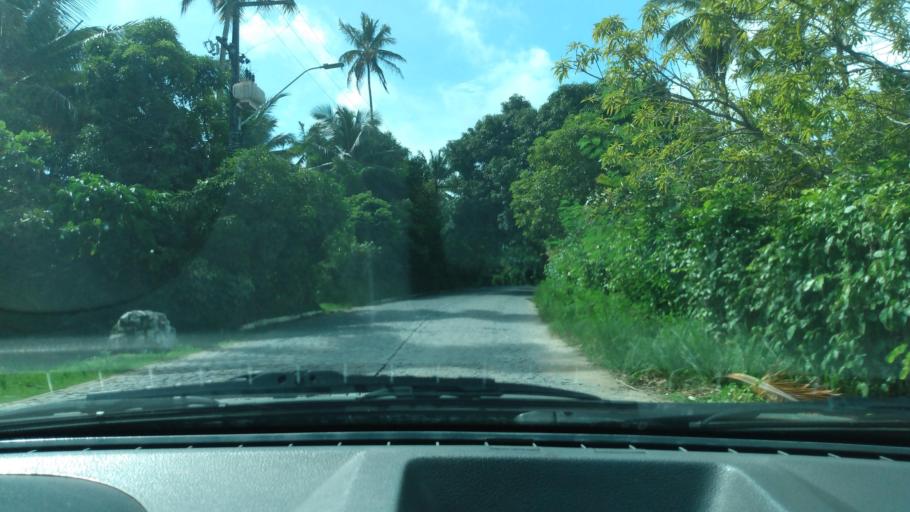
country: BR
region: Pernambuco
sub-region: Cabo De Santo Agostinho
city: Cabo
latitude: -8.3509
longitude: -34.9524
